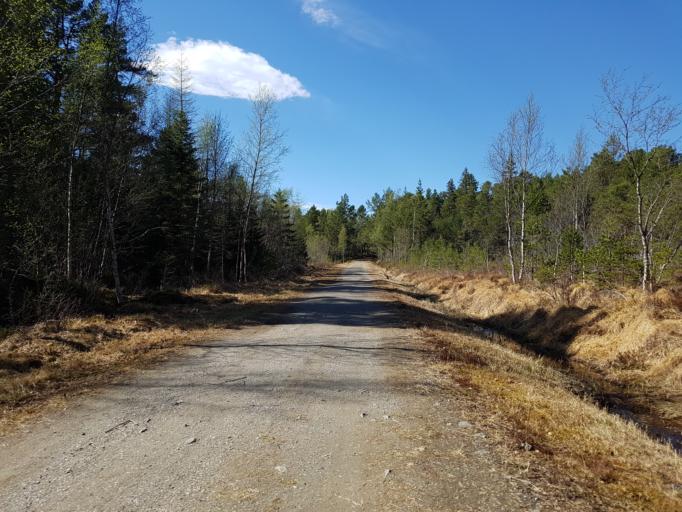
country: NO
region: Sor-Trondelag
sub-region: Trondheim
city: Trondheim
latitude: 63.4400
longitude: 10.3239
